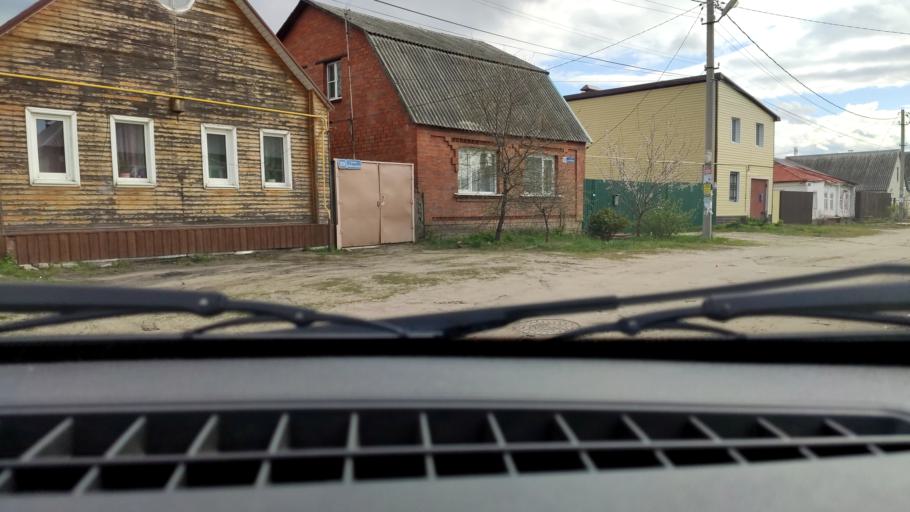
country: RU
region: Voronezj
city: Voronezh
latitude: 51.7297
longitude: 39.2652
